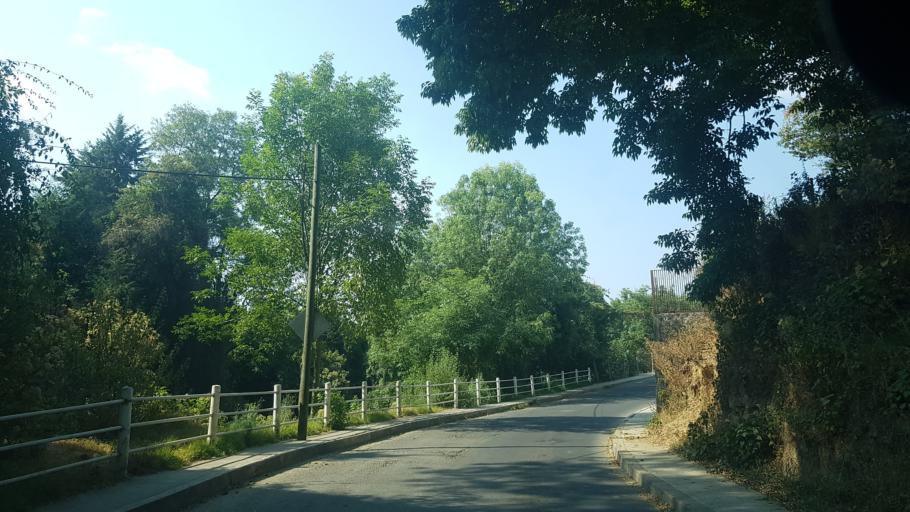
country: MX
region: Morelos
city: Hueyapan
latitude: 18.8886
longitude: -98.6822
